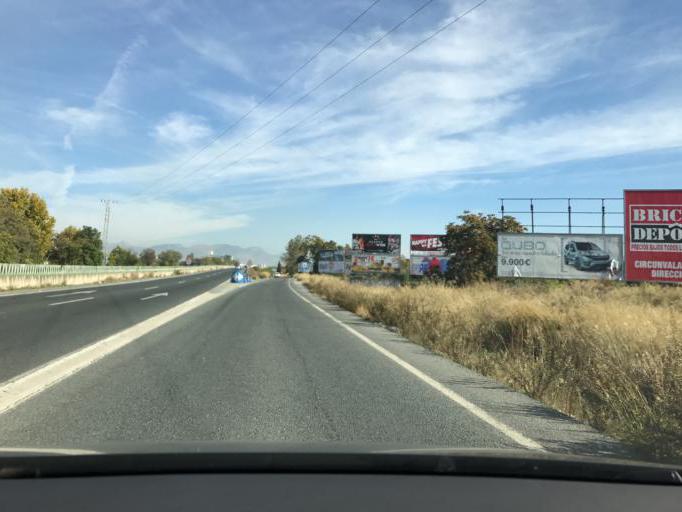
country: ES
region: Andalusia
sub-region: Provincia de Granada
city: Chauchina
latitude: 37.1908
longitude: -3.7289
